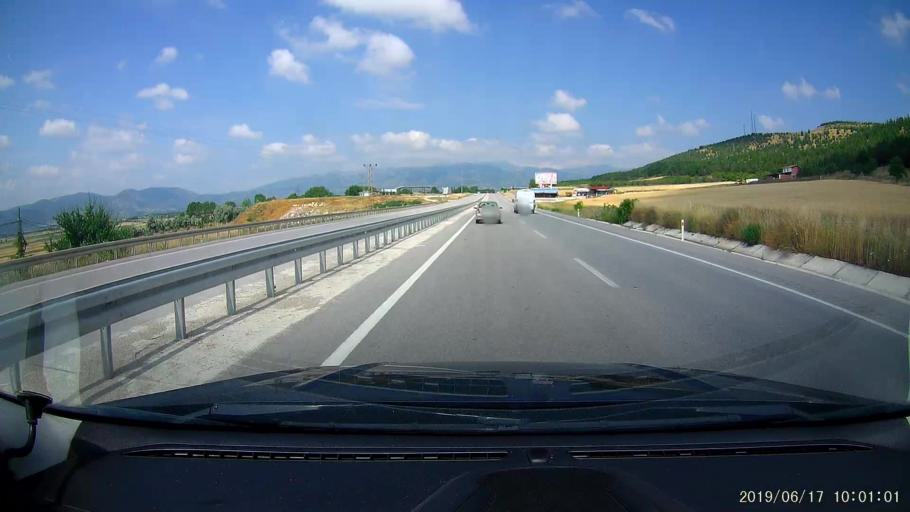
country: TR
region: Amasya
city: Gumushacikoy
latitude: 40.8665
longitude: 35.2748
